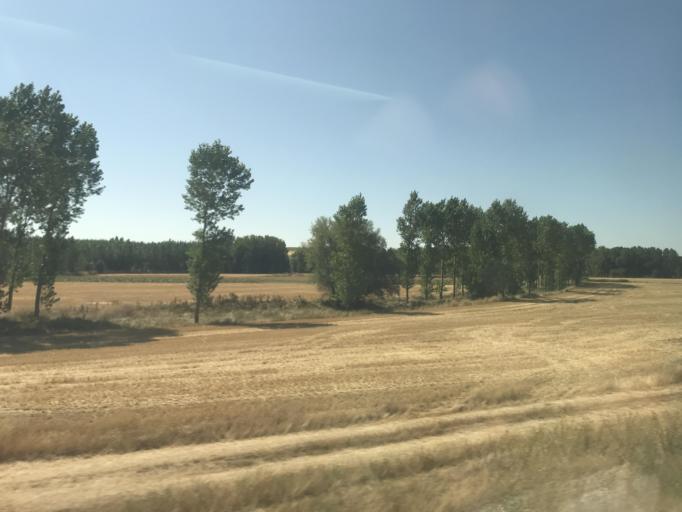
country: ES
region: Castille and Leon
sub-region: Provincia de Burgos
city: Estepar
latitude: 42.2805
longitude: -3.8743
